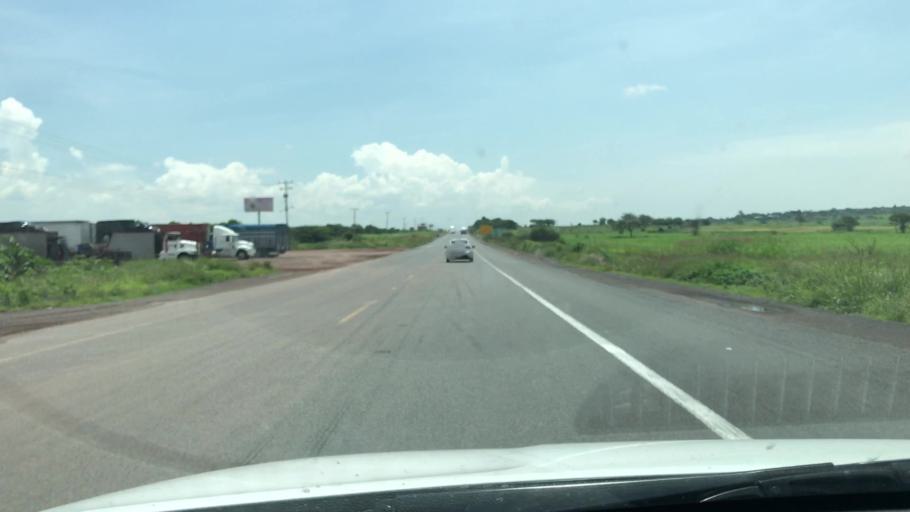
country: MX
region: Jalisco
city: Degollado
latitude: 20.3634
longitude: -102.1411
